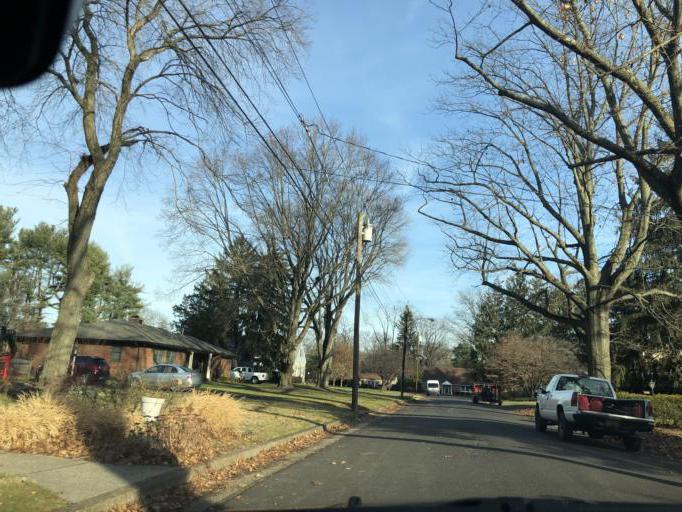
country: US
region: New Jersey
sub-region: Burlington County
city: Moorestown-Lenola
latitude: 39.9605
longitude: -74.9656
